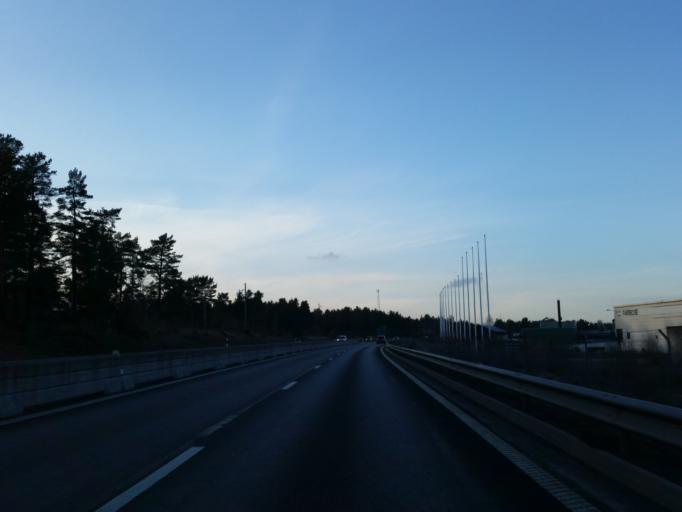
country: SE
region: Kalmar
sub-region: Oskarshamns Kommun
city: Oskarshamn
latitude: 57.3788
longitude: 16.4841
